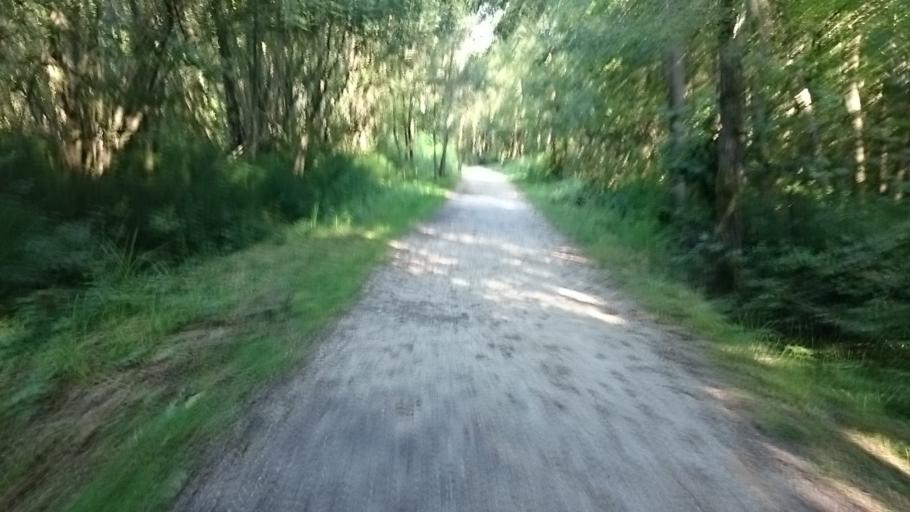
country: IT
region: Veneto
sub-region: Provincia di Belluno
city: Farra d'Alpago
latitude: 46.1241
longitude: 12.3433
